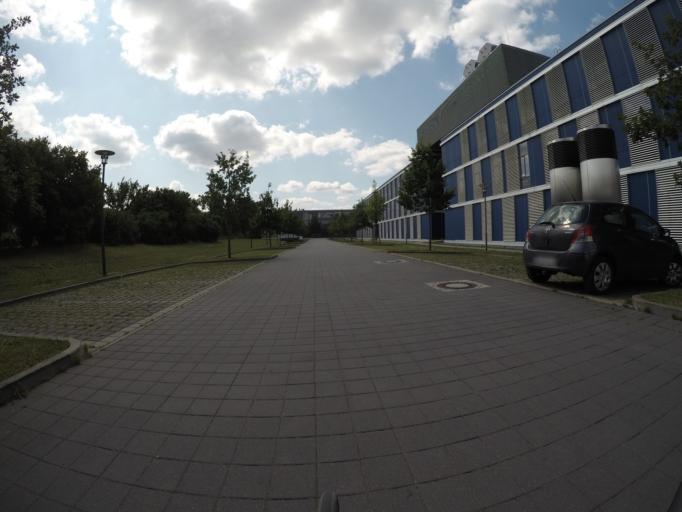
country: DE
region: Brandenburg
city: Werder
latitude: 52.4108
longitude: 12.9760
